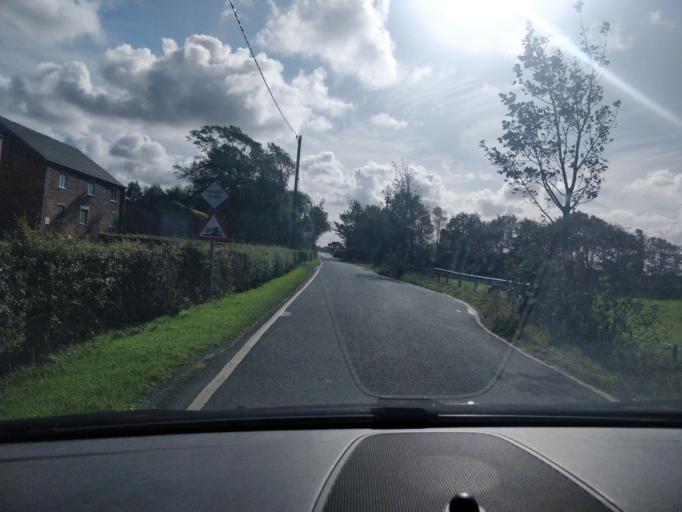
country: GB
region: England
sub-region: Lancashire
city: Banks
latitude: 53.6326
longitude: -2.9432
